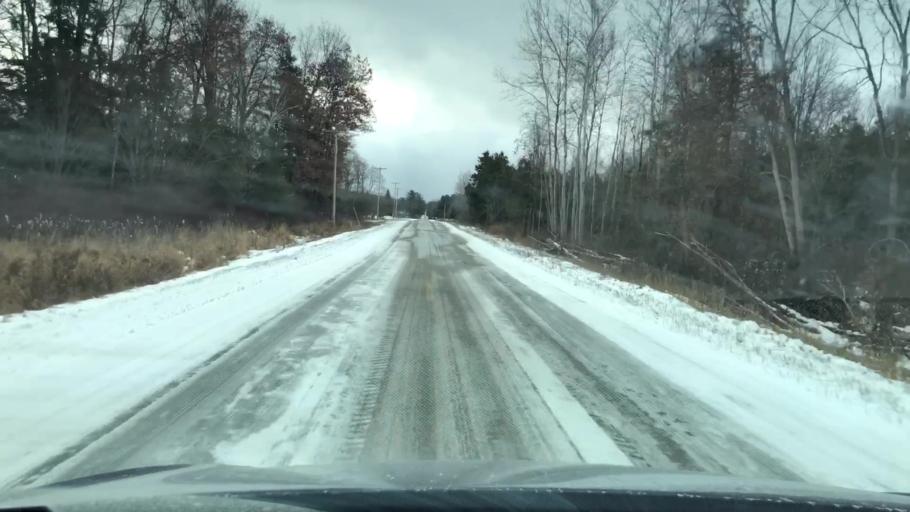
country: US
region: Michigan
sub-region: Antrim County
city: Elk Rapids
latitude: 44.9136
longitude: -85.5155
